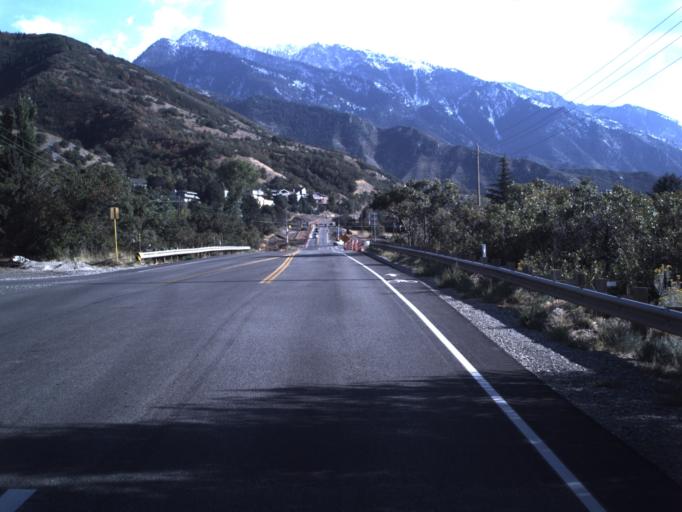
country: US
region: Utah
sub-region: Salt Lake County
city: Granite
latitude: 40.5917
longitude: -111.7948
